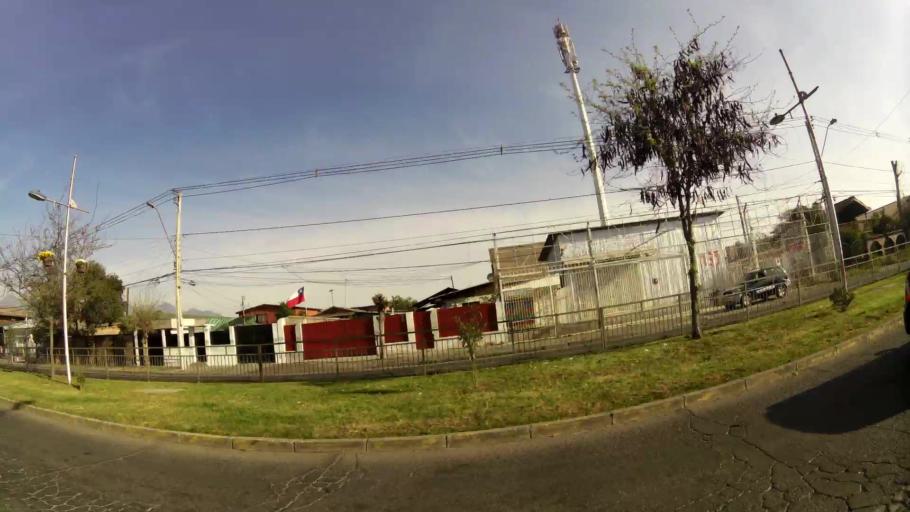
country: CL
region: Santiago Metropolitan
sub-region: Provincia de Santiago
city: La Pintana
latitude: -33.5471
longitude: -70.5857
